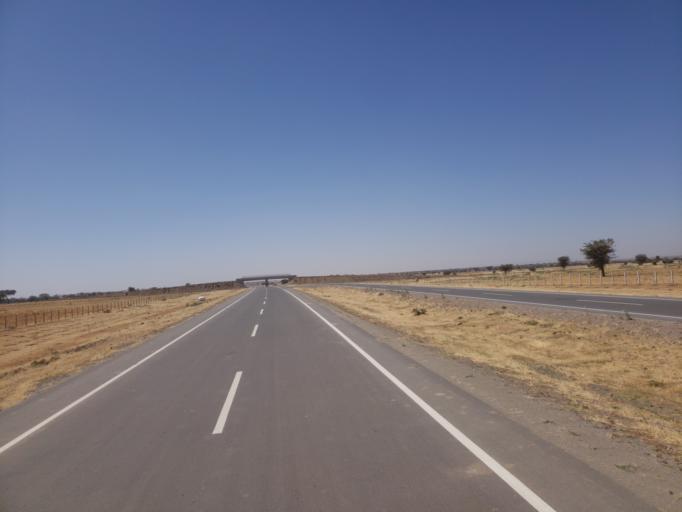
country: ET
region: Oromiya
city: Ziway
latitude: 8.2475
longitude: 38.8861
